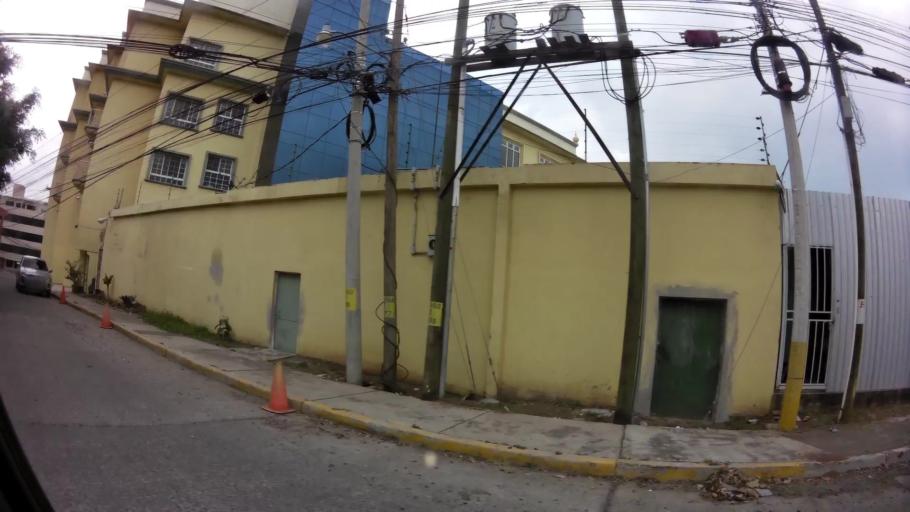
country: HN
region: Francisco Morazan
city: Tegucigalpa
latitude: 14.0913
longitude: -87.1929
